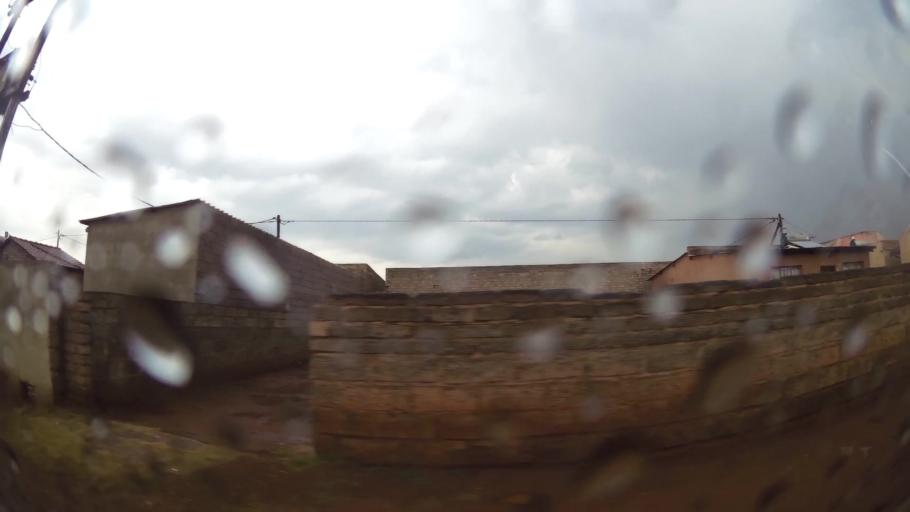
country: ZA
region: Gauteng
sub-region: Ekurhuleni Metropolitan Municipality
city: Germiston
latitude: -26.3777
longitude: 28.1509
